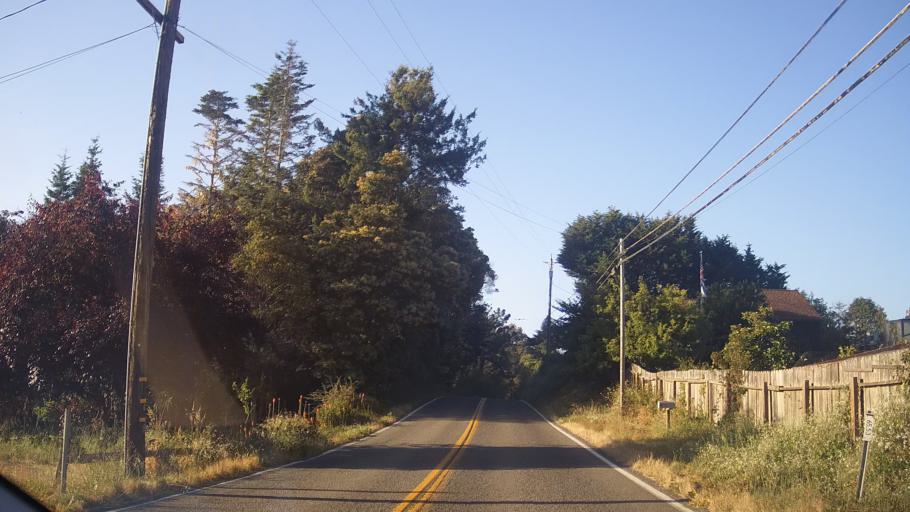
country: US
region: California
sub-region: Mendocino County
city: Fort Bragg
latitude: 39.4955
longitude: -123.7807
